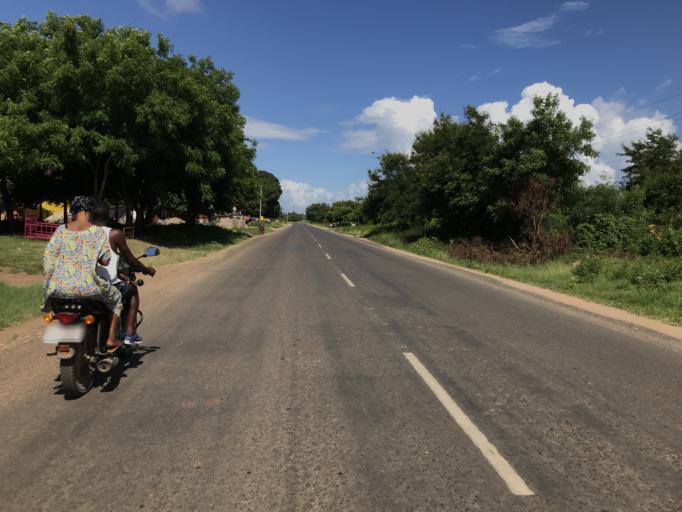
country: TZ
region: Dar es Salaam
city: Dar es Salaam
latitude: -6.8719
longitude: 39.4063
